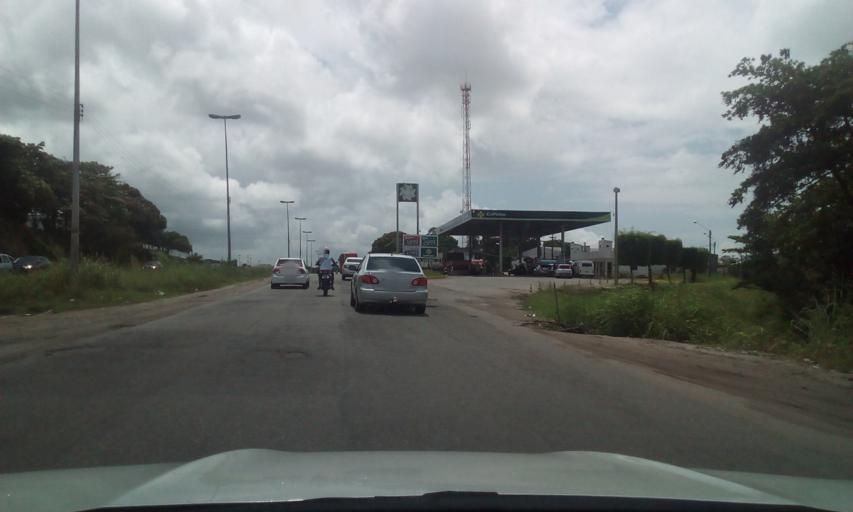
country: BR
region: Pernambuco
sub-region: Recife
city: Recife
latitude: -8.0794
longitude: -34.9430
